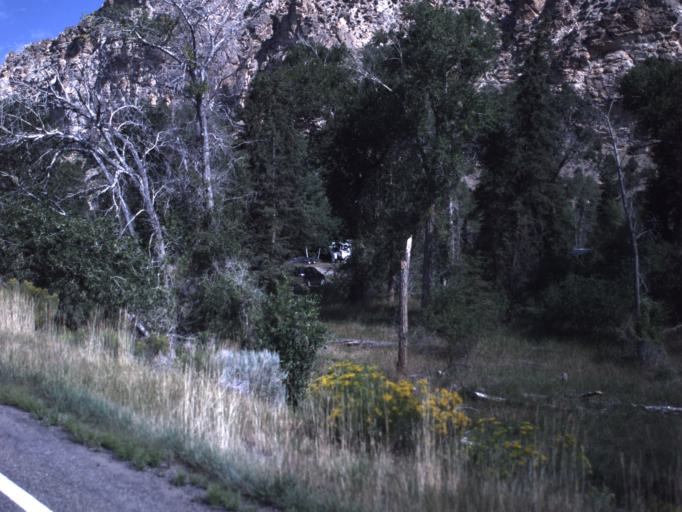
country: US
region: Utah
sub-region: Daggett County
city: Manila
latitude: 40.9248
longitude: -109.7130
